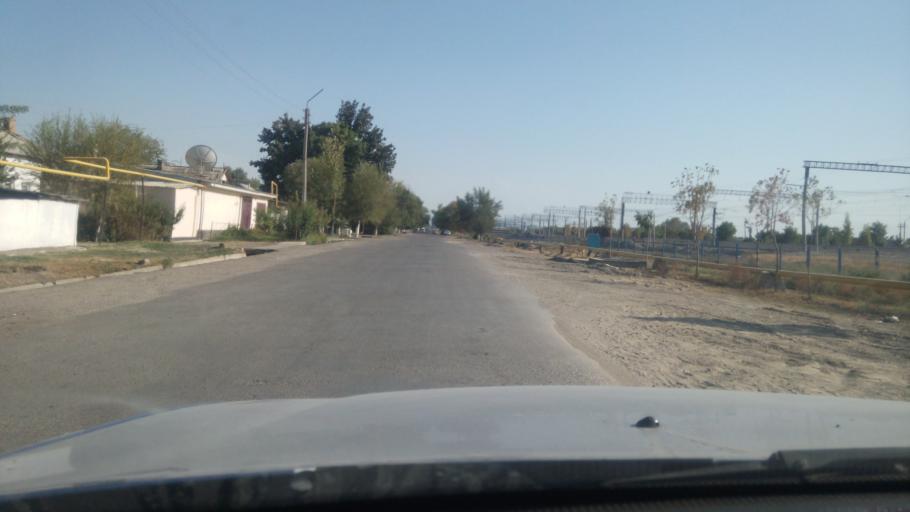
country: UZ
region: Sirdaryo
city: Guliston
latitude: 40.5048
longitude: 68.7627
